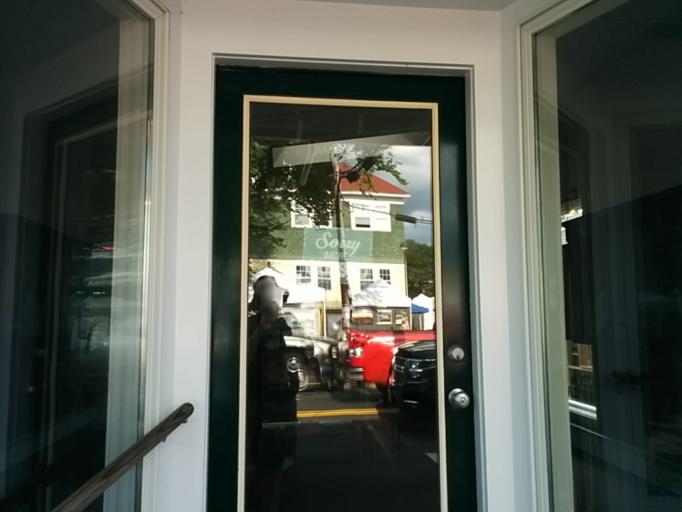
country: US
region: Maine
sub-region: Hancock County
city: Tremont
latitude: 44.2803
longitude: -68.3262
